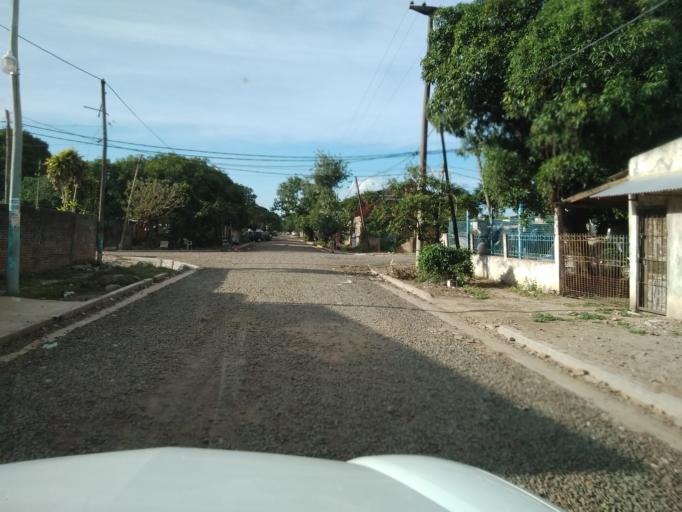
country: AR
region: Corrientes
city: Corrientes
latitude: -27.4907
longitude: -58.8460
